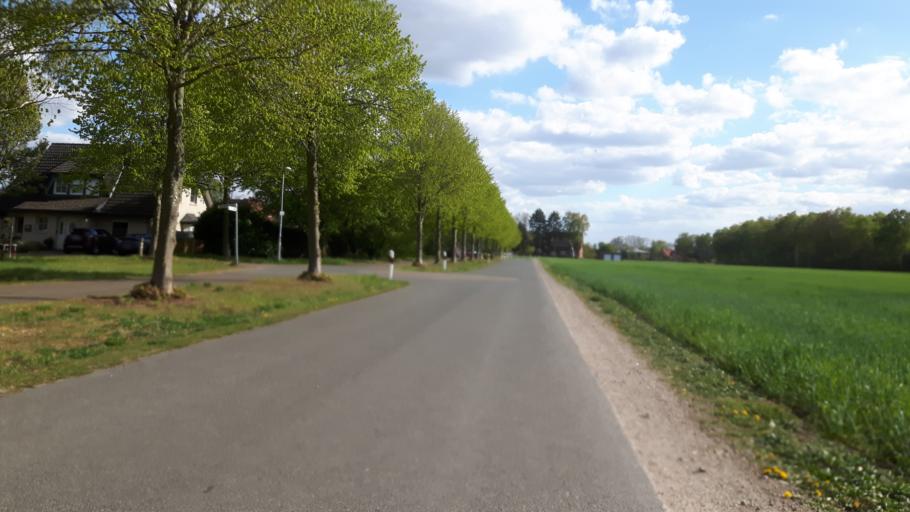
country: DE
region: Lower Saxony
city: Kirchseelte
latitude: 52.9955
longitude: 8.6891
